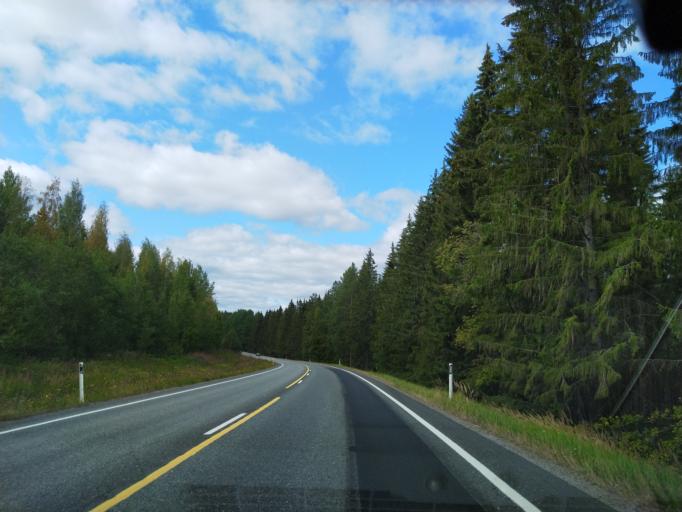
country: FI
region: Haeme
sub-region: Haemeenlinna
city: Tervakoski
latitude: 60.7444
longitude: 24.6663
